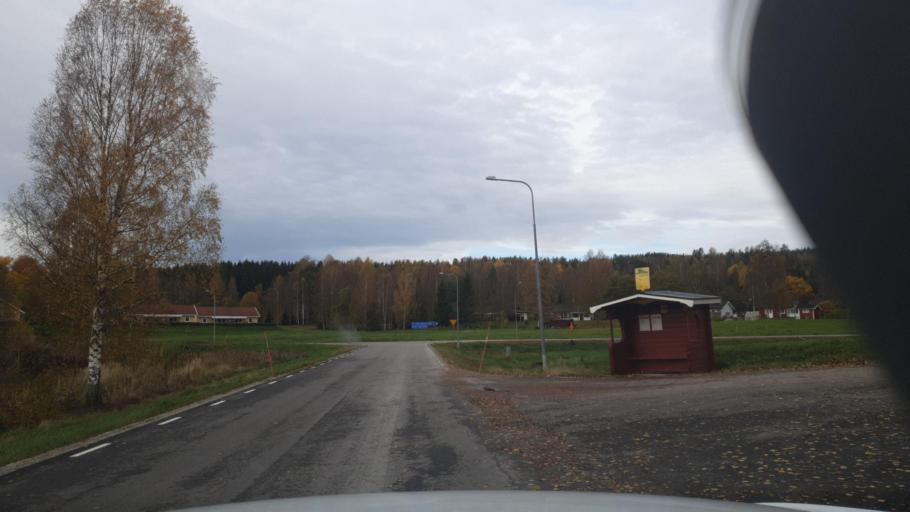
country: SE
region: Vaermland
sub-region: Arvika Kommun
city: Arvika
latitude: 59.7506
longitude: 12.8240
